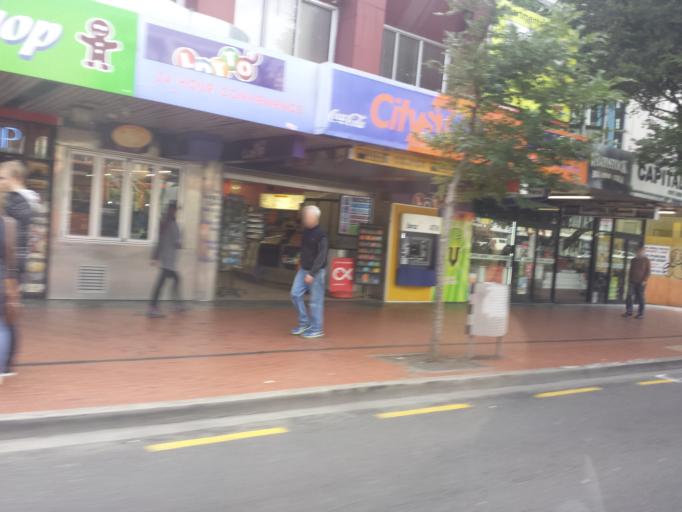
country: NZ
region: Wellington
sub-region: Wellington City
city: Wellington
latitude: -41.2915
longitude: 174.7773
